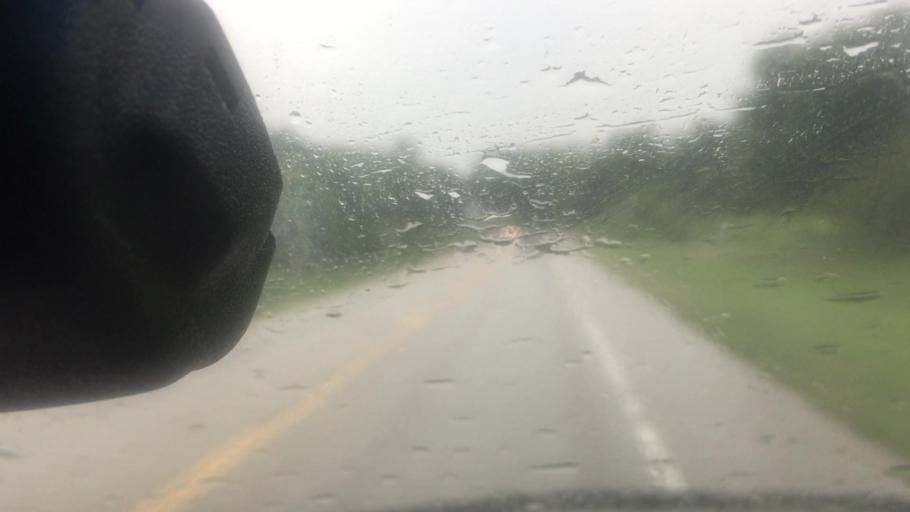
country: US
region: Illinois
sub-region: Madison County
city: Edwardsville
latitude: 38.8282
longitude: -89.9353
